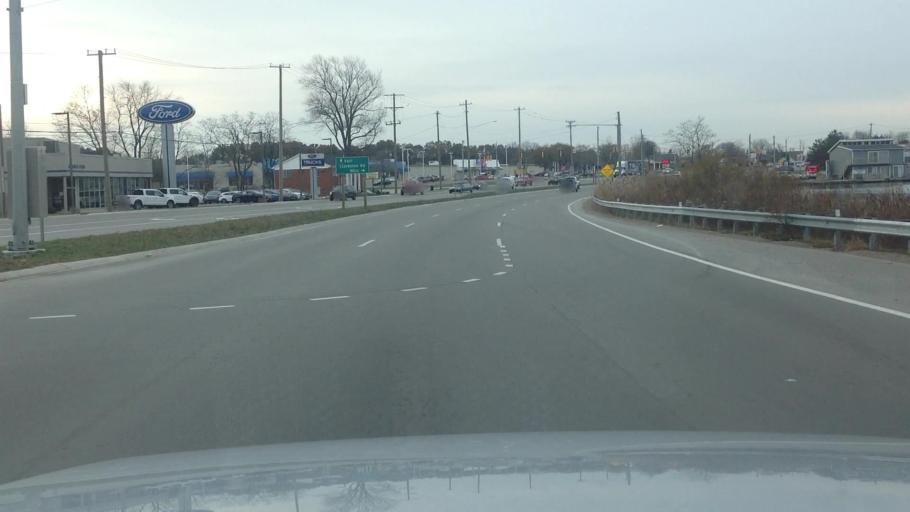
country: US
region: Michigan
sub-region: Oakland County
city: Lake Orion
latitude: 42.7698
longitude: -83.2386
